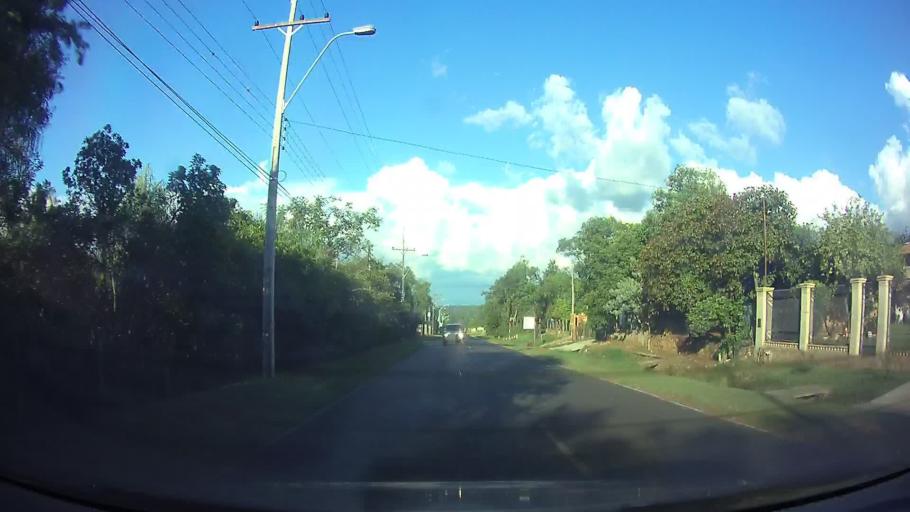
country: PY
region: Cordillera
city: Emboscada
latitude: -25.1926
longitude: -57.3126
